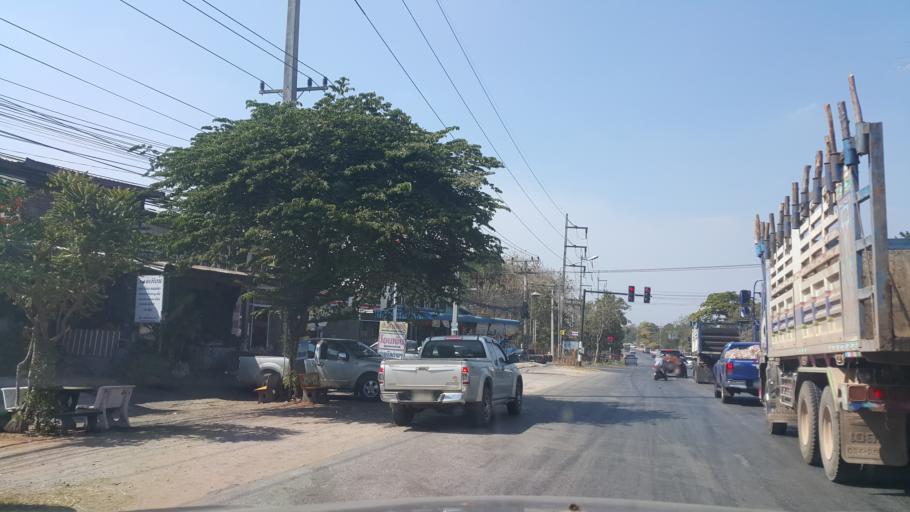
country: TH
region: Nakhon Ratchasima
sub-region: Amphoe Kaeng Sanam Nang
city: Kaeng Sanam Nang
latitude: 15.7498
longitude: 102.2571
